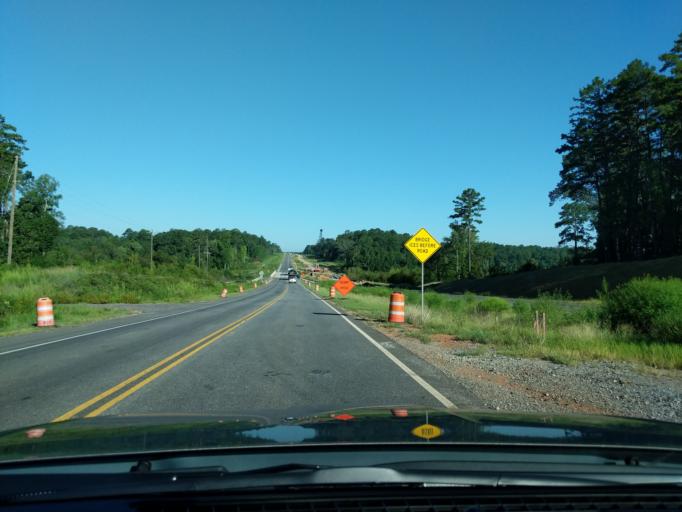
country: US
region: Georgia
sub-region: McDuffie County
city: Thomson
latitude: 33.5800
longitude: -82.5284
